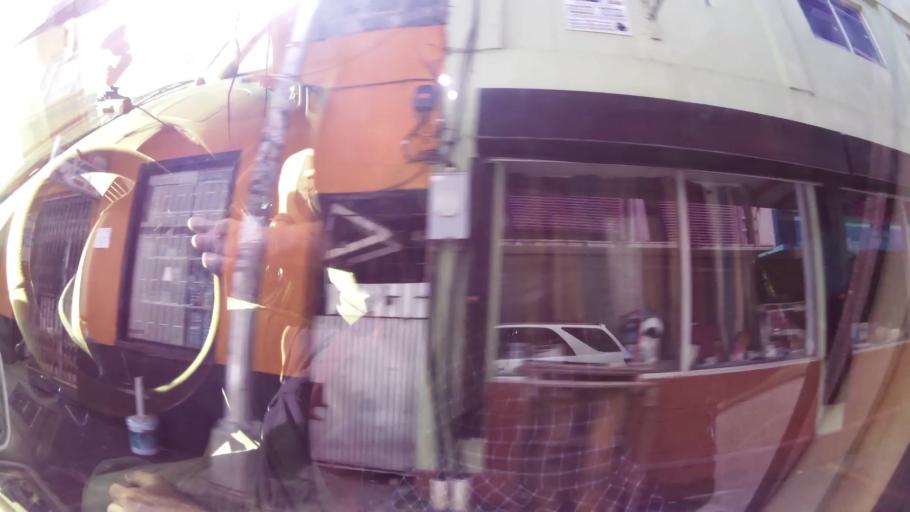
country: VC
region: Saint George
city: Kingstown
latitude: 13.1542
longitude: -61.2249
